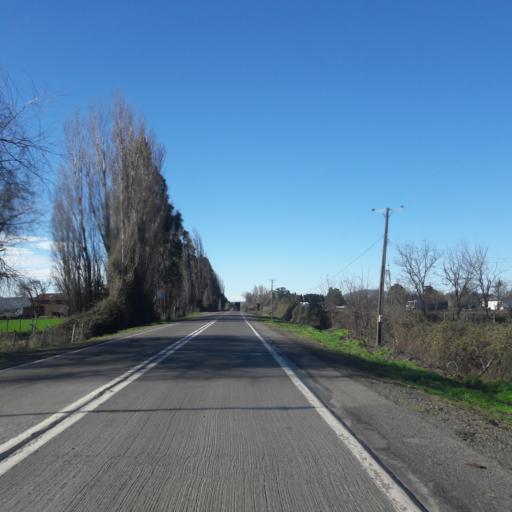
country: CL
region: Araucania
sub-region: Provincia de Malleco
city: Angol
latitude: -37.7701
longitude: -72.5532
